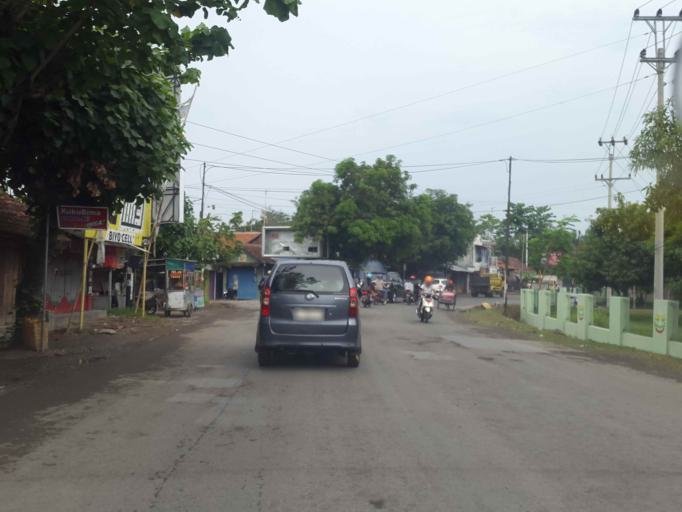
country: ID
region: Central Java
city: Adiwerna
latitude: -6.9426
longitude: 109.1242
